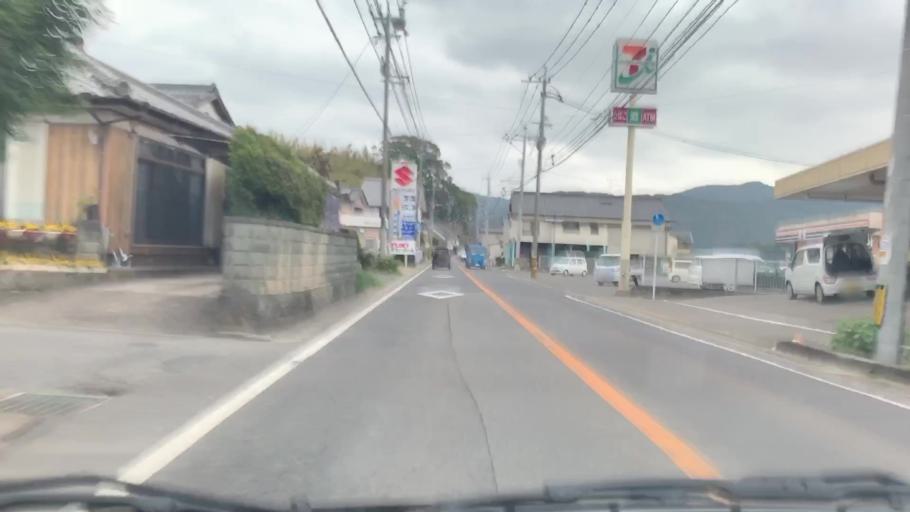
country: JP
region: Saga Prefecture
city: Kashima
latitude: 33.1342
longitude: 130.0622
